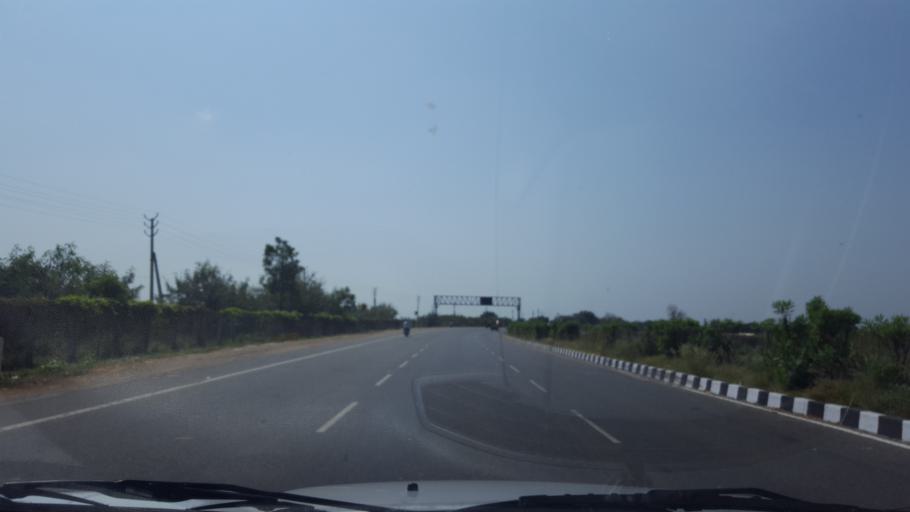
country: IN
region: Andhra Pradesh
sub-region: Prakasam
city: Addanki
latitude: 15.7457
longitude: 80.0276
